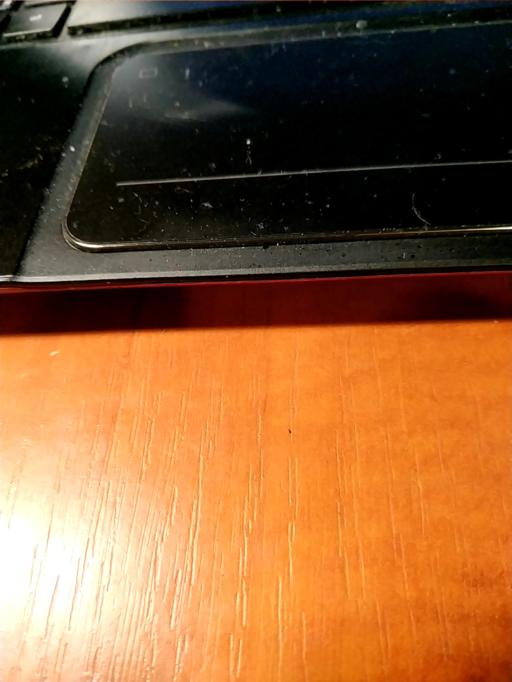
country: RU
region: Lipetsk
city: Chaplygin
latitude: 53.3197
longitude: 40.0702
